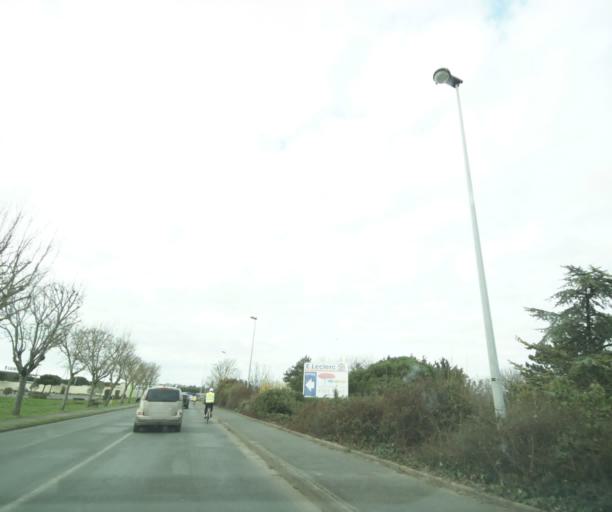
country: FR
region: Poitou-Charentes
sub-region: Departement de la Charente-Maritime
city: La Rochelle
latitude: 46.1724
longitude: -1.1650
